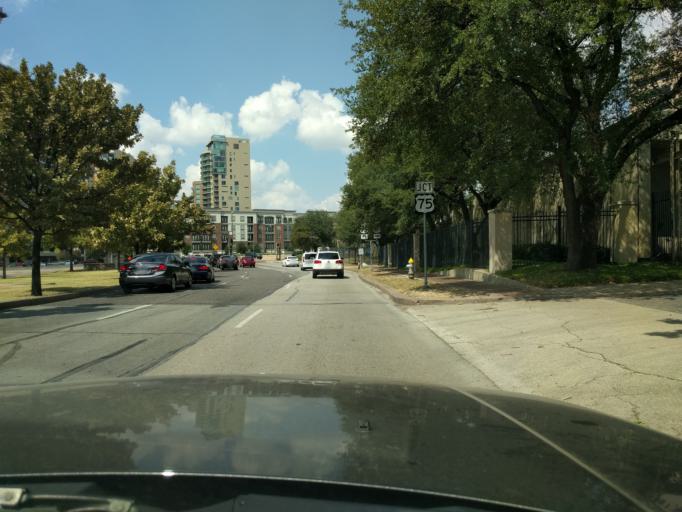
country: US
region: Texas
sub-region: Dallas County
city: Highland Park
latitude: 32.8069
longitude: -96.7919
